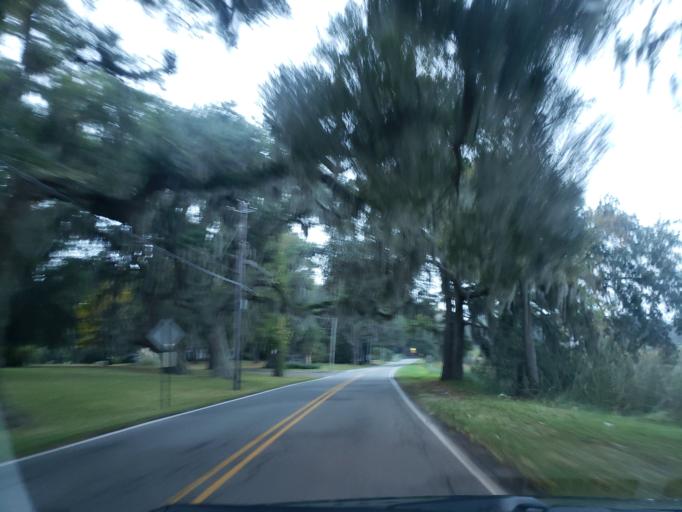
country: US
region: Georgia
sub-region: Chatham County
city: Isle of Hope
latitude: 32.0065
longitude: -81.0651
